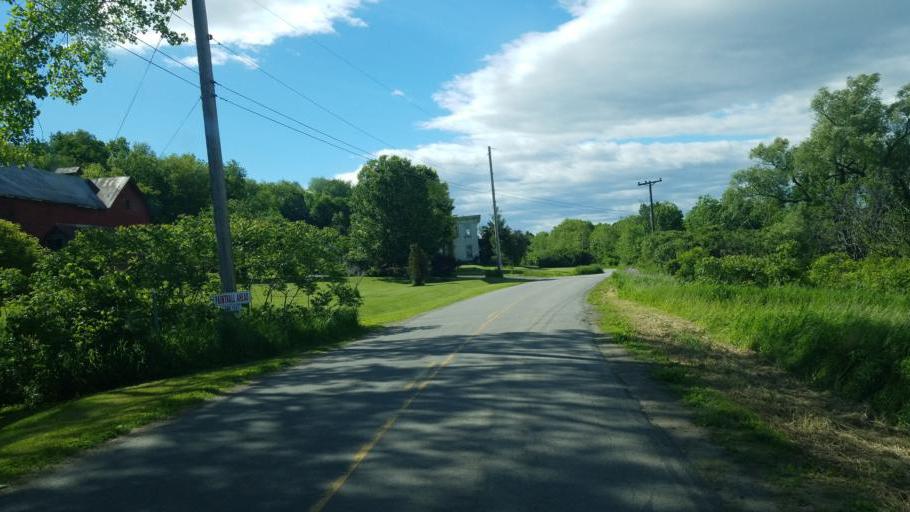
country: US
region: New York
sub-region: Montgomery County
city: Saint Johnsville
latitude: 42.9706
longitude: -74.6494
